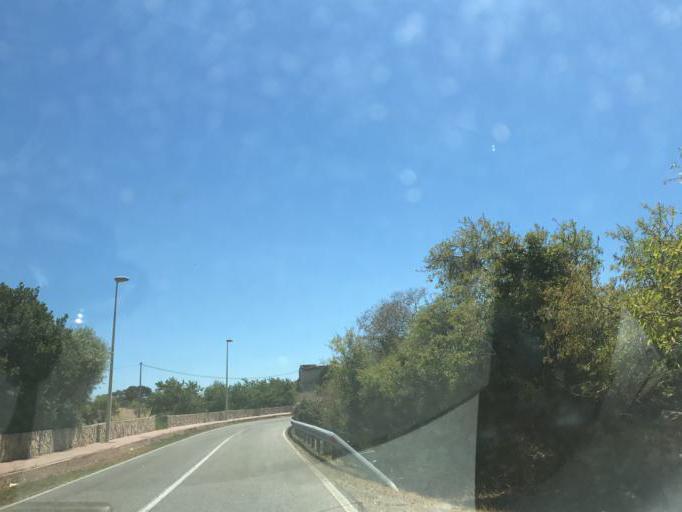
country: IT
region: Sardinia
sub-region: Provincia di Olbia-Tempio
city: Telti
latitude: 40.8783
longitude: 9.3470
